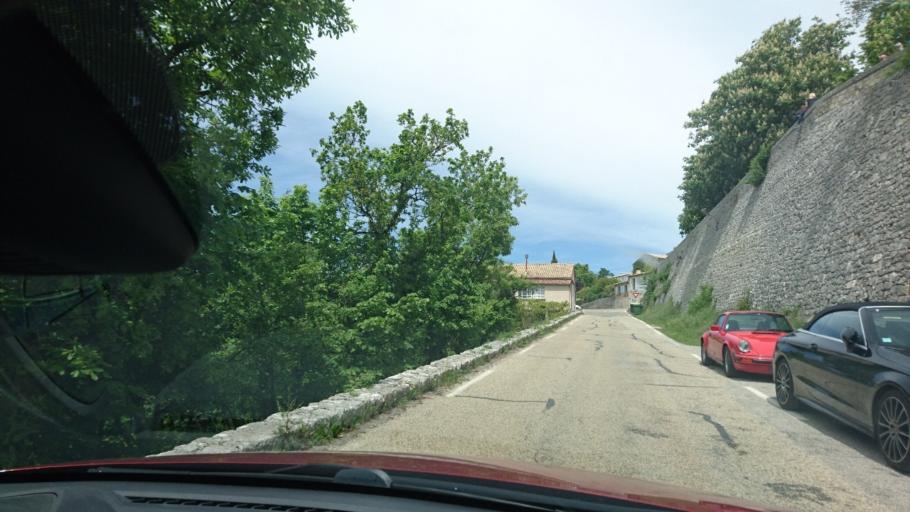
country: FR
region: Provence-Alpes-Cote d'Azur
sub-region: Departement du Vaucluse
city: Sault
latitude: 44.0928
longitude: 5.4075
